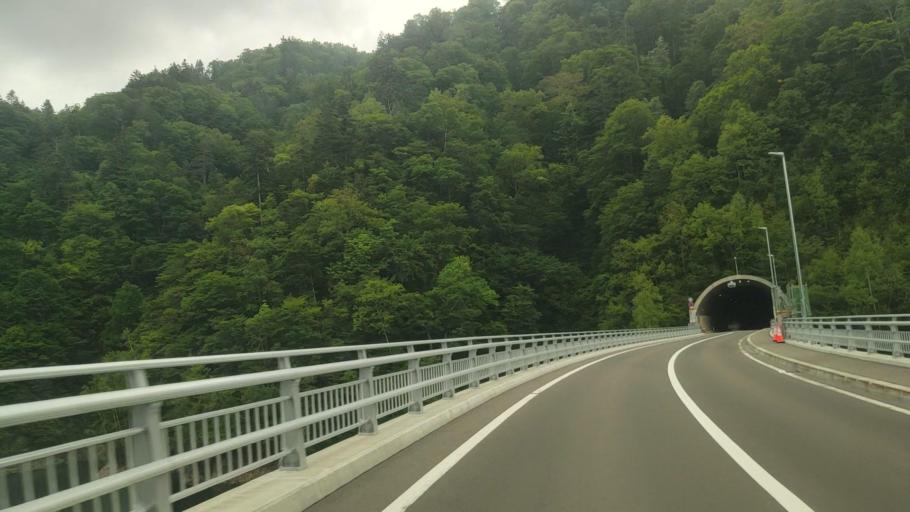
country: JP
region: Hokkaido
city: Sapporo
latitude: 42.9895
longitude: 141.1639
